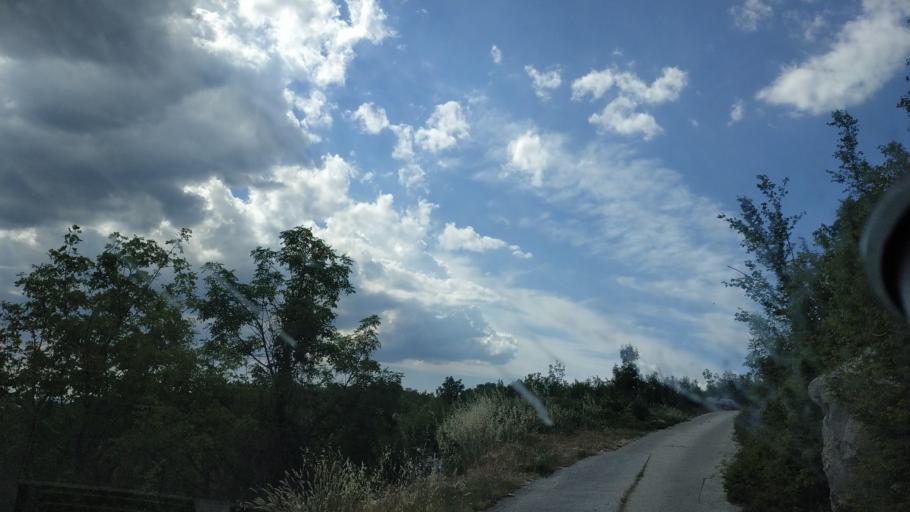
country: HR
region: Splitsko-Dalmatinska
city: Dugopolje
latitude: 43.5673
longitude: 16.6532
